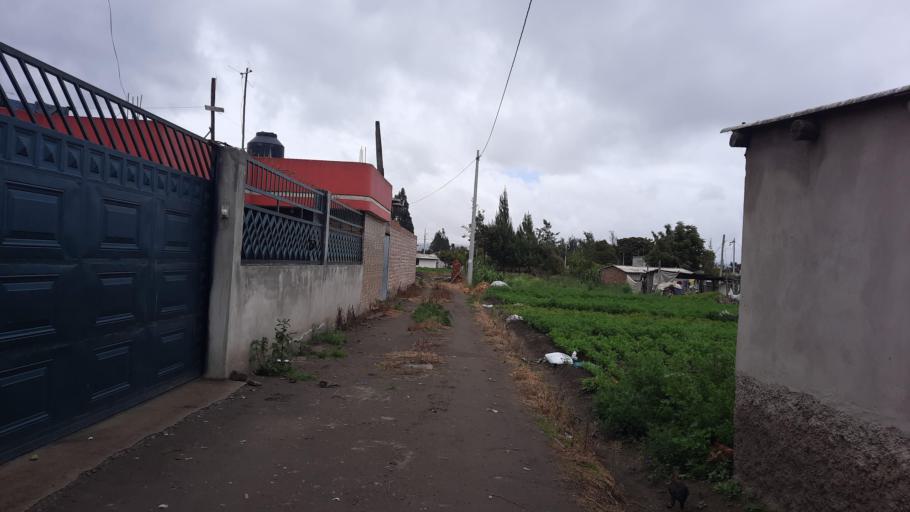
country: EC
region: Chimborazo
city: Riobamba
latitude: -1.6882
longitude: -78.6689
